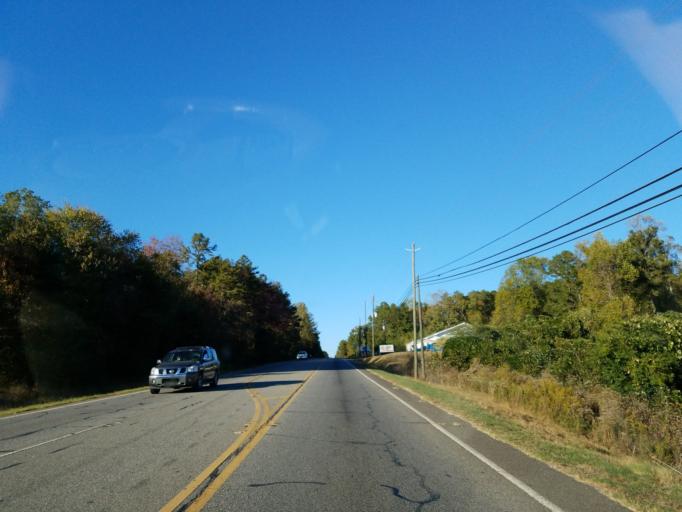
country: US
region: Georgia
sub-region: Cherokee County
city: Ball Ground
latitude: 34.3484
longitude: -84.3798
